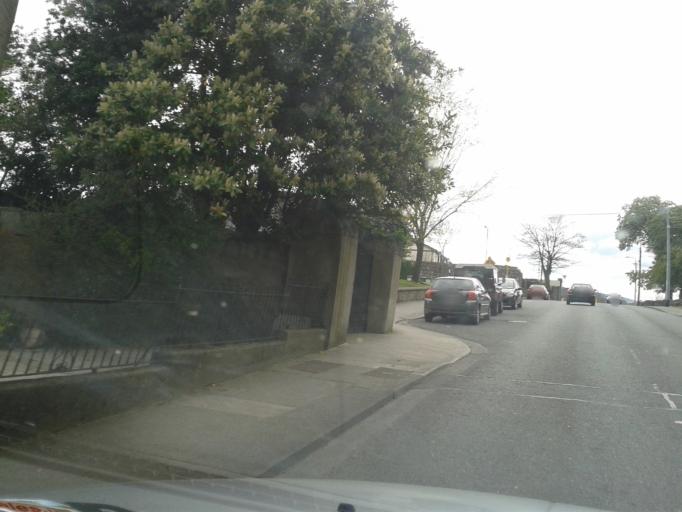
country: IE
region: Leinster
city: Monkstown
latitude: 53.2868
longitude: -6.1590
